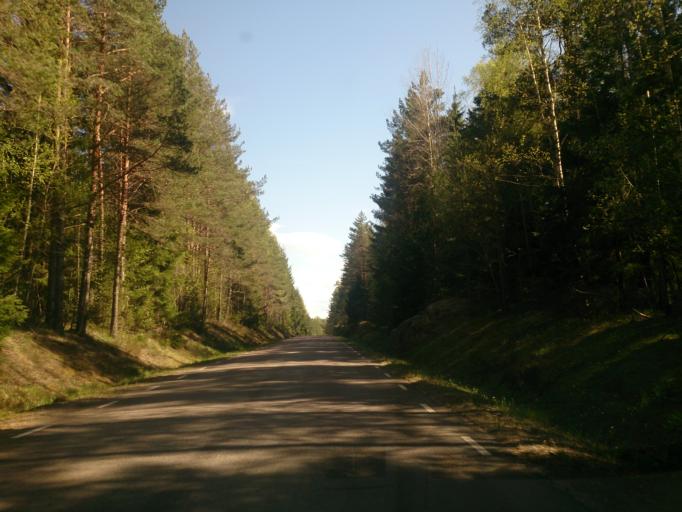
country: SE
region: OEstergoetland
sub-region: Linkopings Kommun
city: Ljungsbro
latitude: 58.6182
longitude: 15.4685
